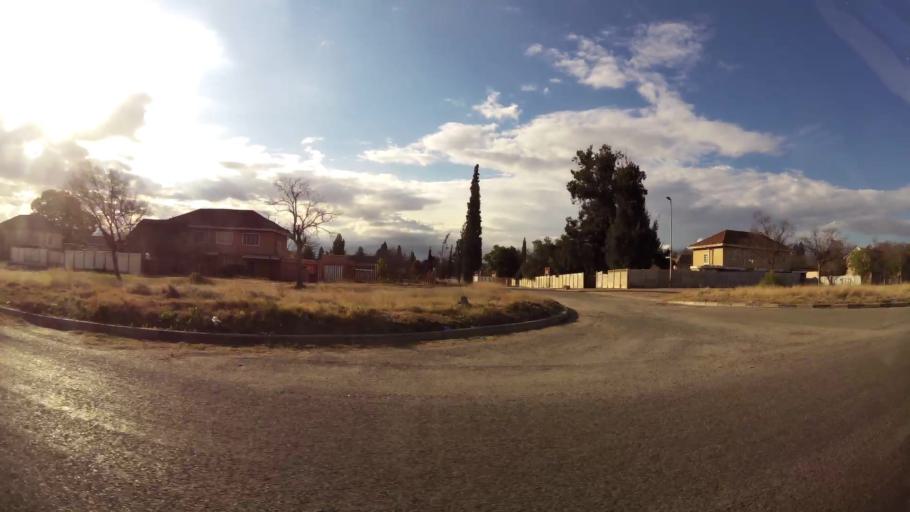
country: ZA
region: Orange Free State
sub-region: Lejweleputswa District Municipality
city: Welkom
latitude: -27.9872
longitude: 26.7080
